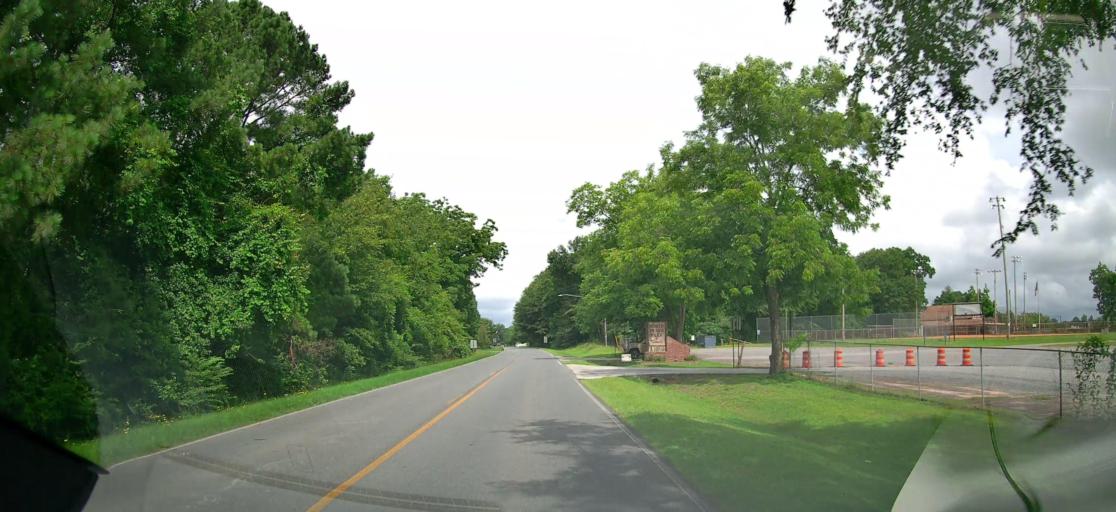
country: US
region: Georgia
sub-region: Peach County
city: Byron
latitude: 32.6456
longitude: -83.7498
